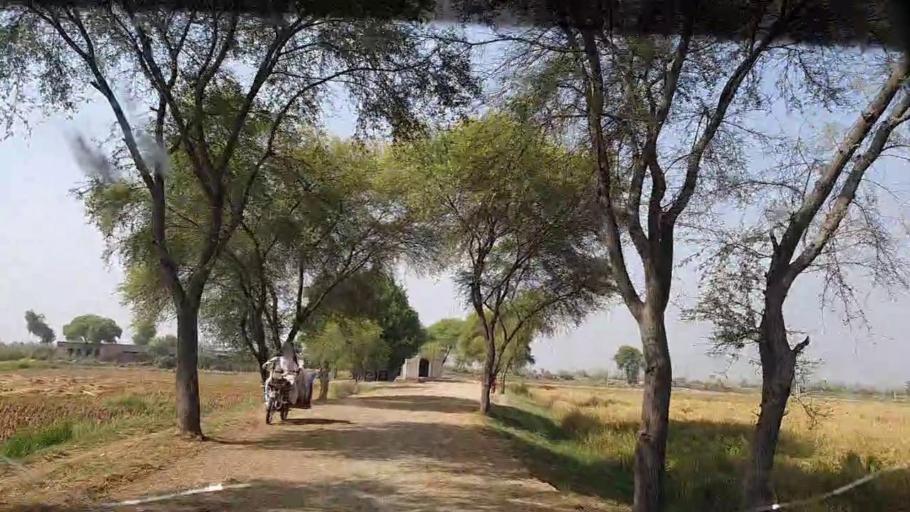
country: PK
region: Sindh
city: Shikarpur
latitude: 28.1159
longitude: 68.6568
